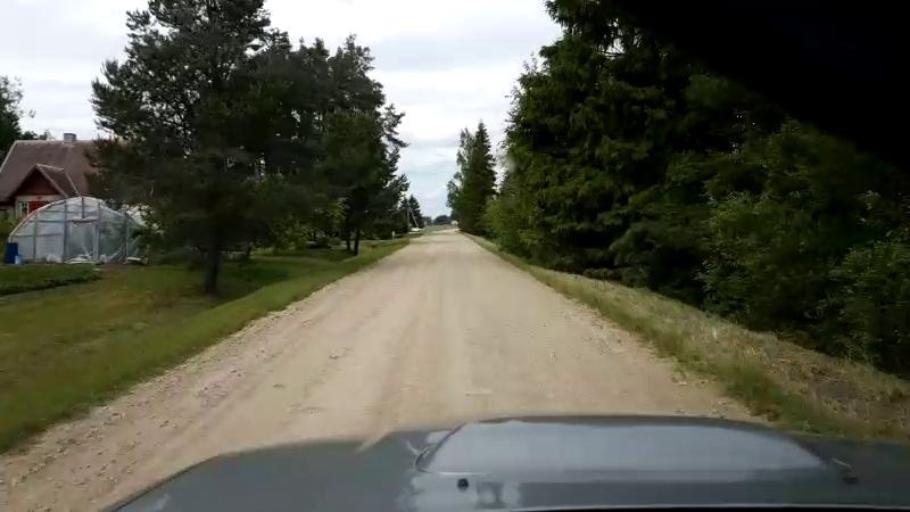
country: EE
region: Paernumaa
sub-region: Halinga vald
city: Parnu-Jaagupi
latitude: 58.5250
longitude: 24.5853
